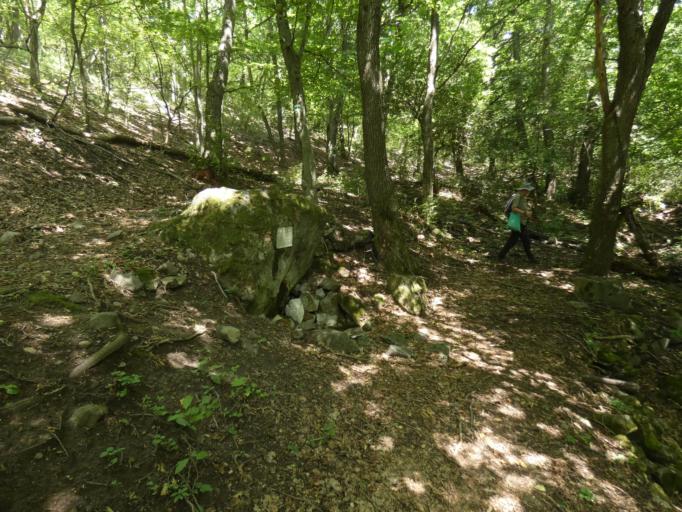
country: HU
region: Borsod-Abauj-Zemplen
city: Gonc
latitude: 48.4049
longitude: 21.3018
